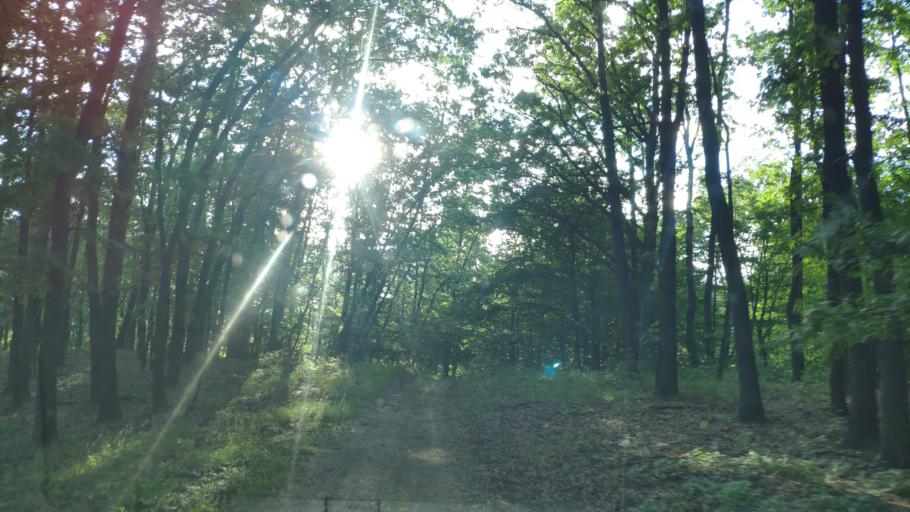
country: HU
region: Borsod-Abauj-Zemplen
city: Arlo
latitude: 48.2447
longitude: 20.1374
